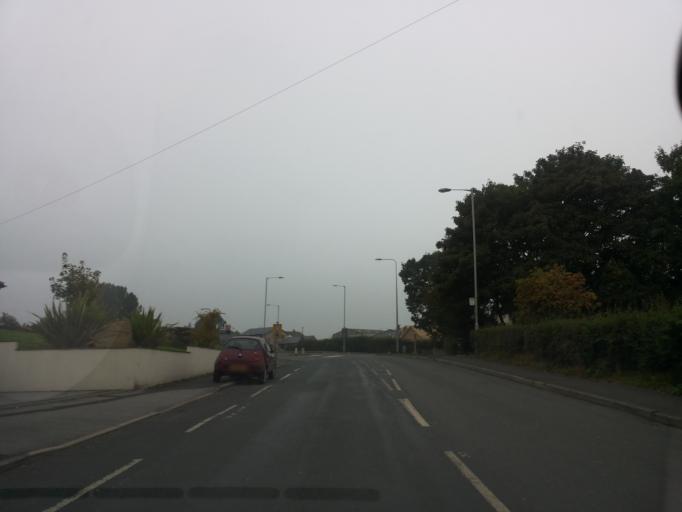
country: GB
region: England
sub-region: Lancashire
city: Billington
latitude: 53.8147
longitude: -2.4266
